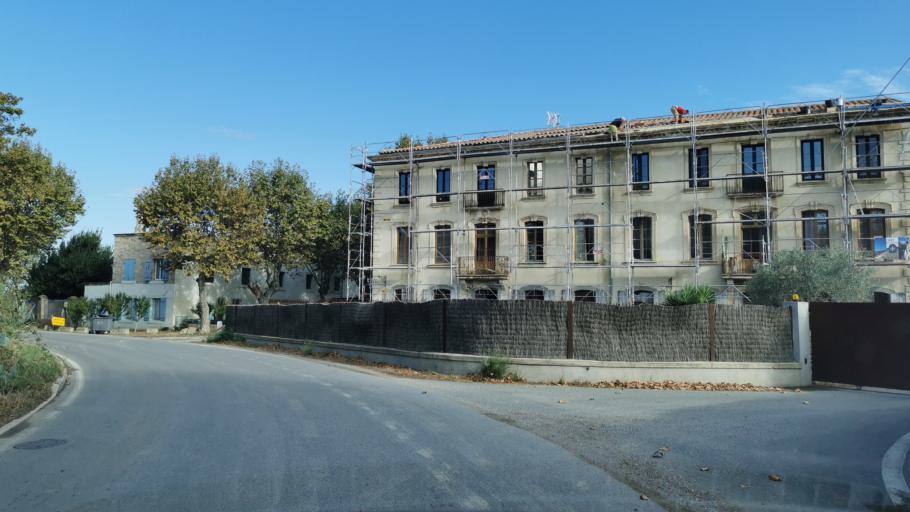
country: FR
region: Languedoc-Roussillon
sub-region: Departement de l'Aude
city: Gruissan
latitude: 43.1299
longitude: 3.0314
